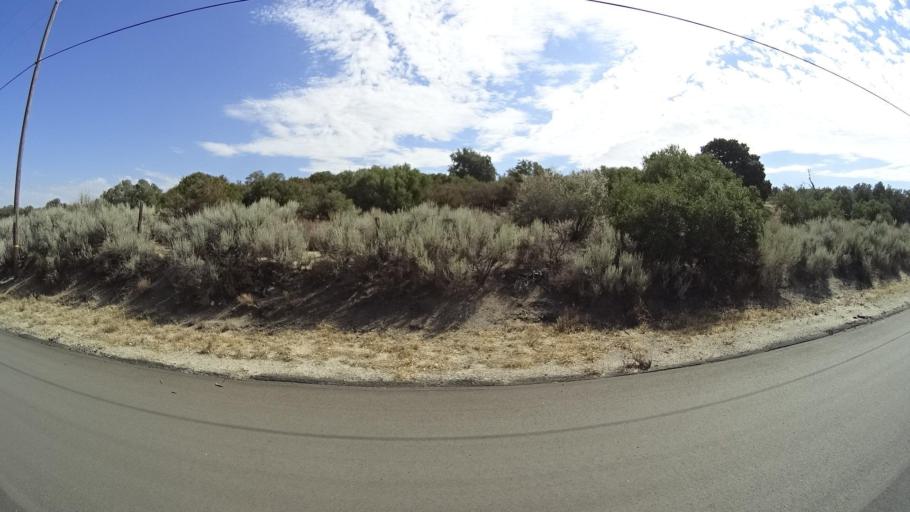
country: US
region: California
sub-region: San Diego County
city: Campo
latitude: 32.6994
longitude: -116.2964
